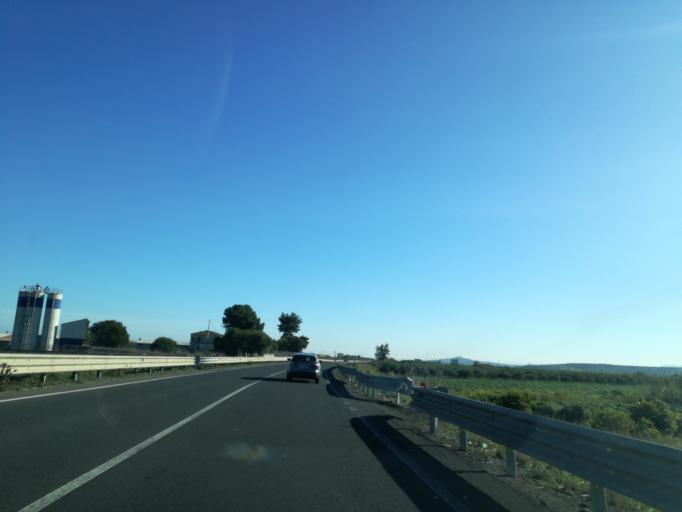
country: IT
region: Sicily
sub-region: Catania
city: Palagonia
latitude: 37.3815
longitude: 14.7564
